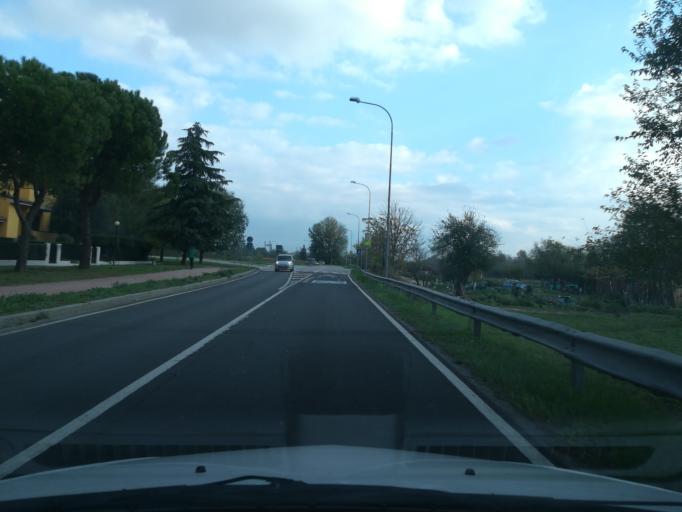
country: IT
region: Emilia-Romagna
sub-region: Provincia di Bologna
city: Imola
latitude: 44.3498
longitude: 11.7325
